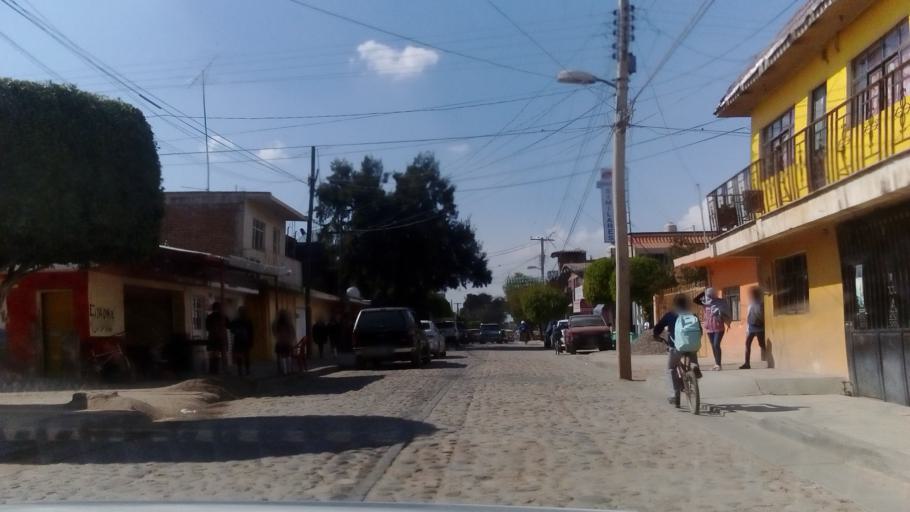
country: MX
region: Guanajuato
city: Duarte
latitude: 21.0865
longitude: -101.5221
